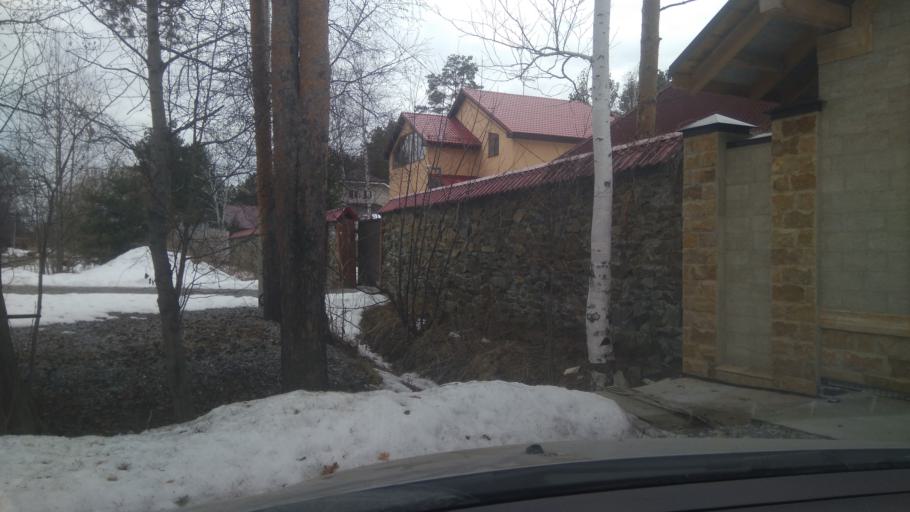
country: RU
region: Sverdlovsk
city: Severka
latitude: 56.8541
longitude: 60.3846
